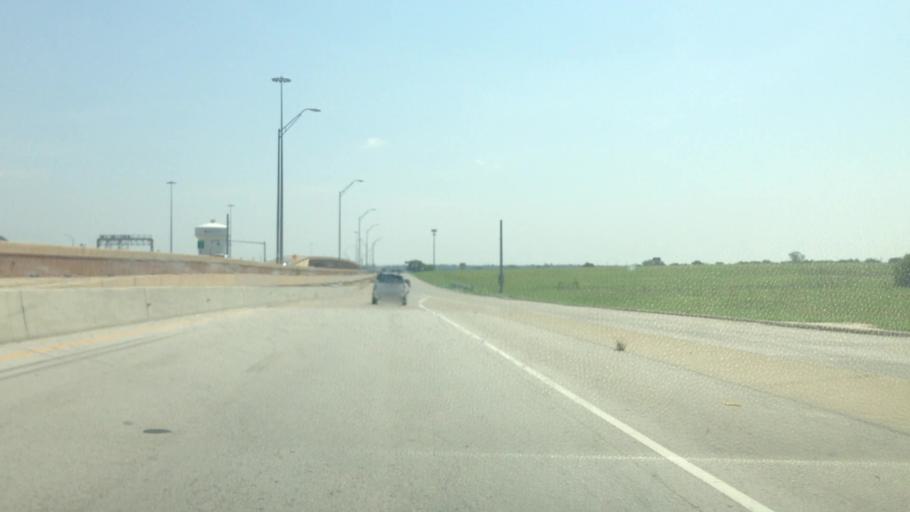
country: US
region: Texas
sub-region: Tarrant County
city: Watauga
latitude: 32.8390
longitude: -97.2870
